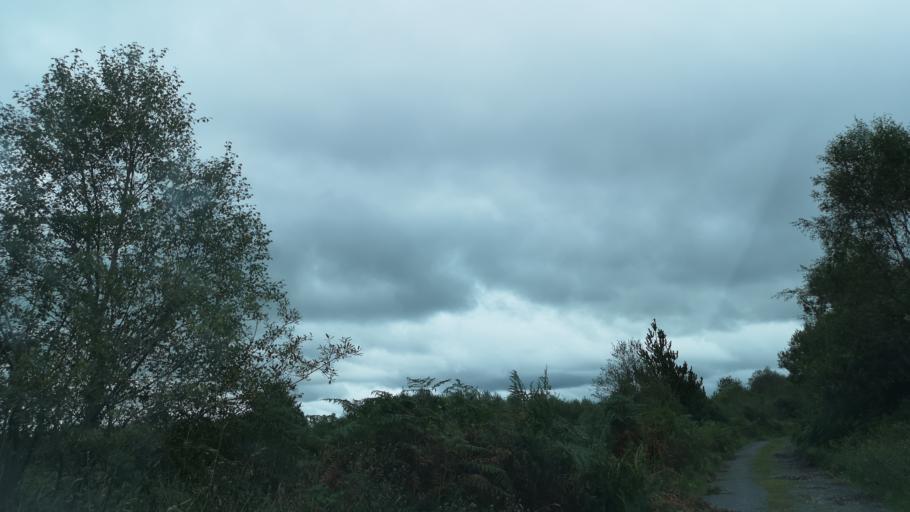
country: IE
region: Connaught
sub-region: County Galway
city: Athenry
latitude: 53.3026
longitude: -8.6536
